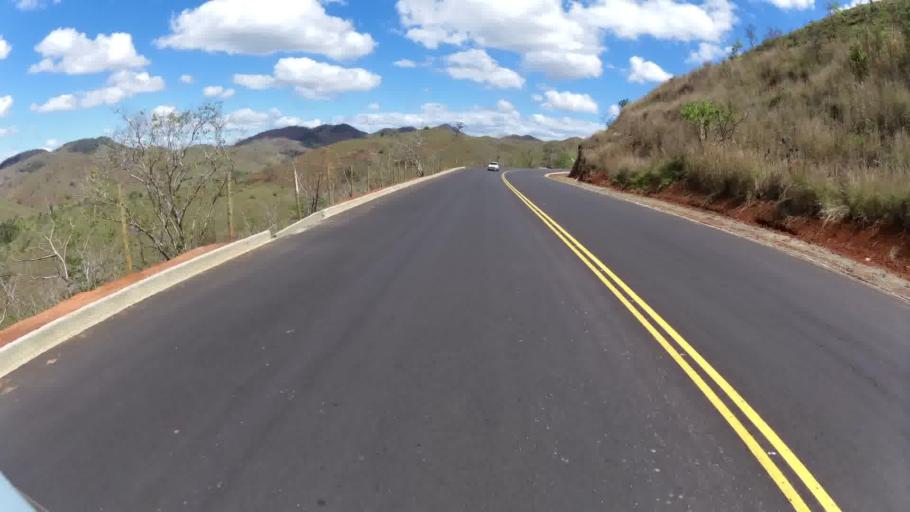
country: BR
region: Rio de Janeiro
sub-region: Itaperuna
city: Itaperuna
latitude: -21.2890
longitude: -41.8013
